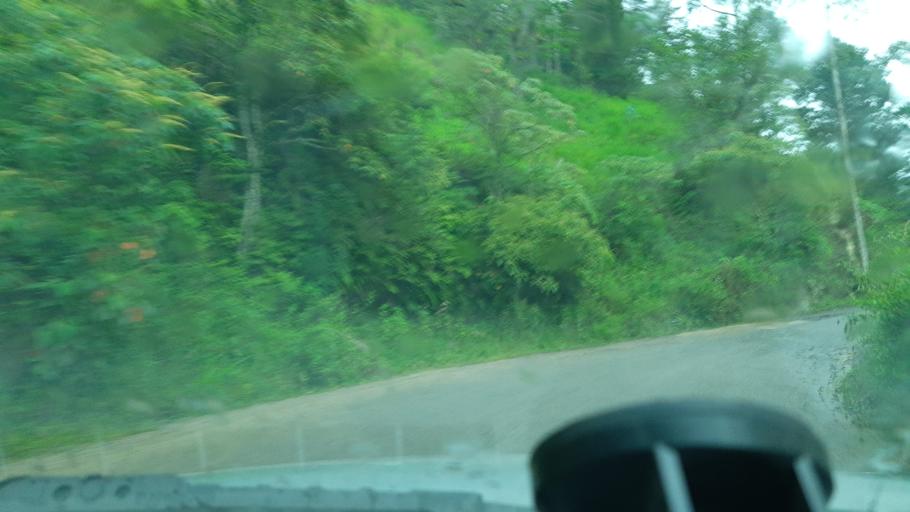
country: CO
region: Boyaca
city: Chinavita
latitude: 5.2161
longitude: -73.3935
